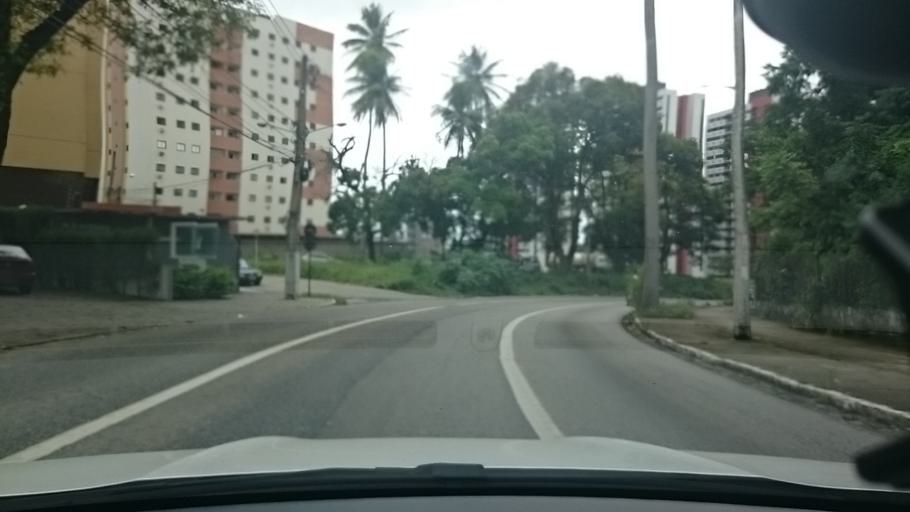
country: BR
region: Paraiba
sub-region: Joao Pessoa
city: Joao Pessoa
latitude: -7.1319
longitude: -34.8610
